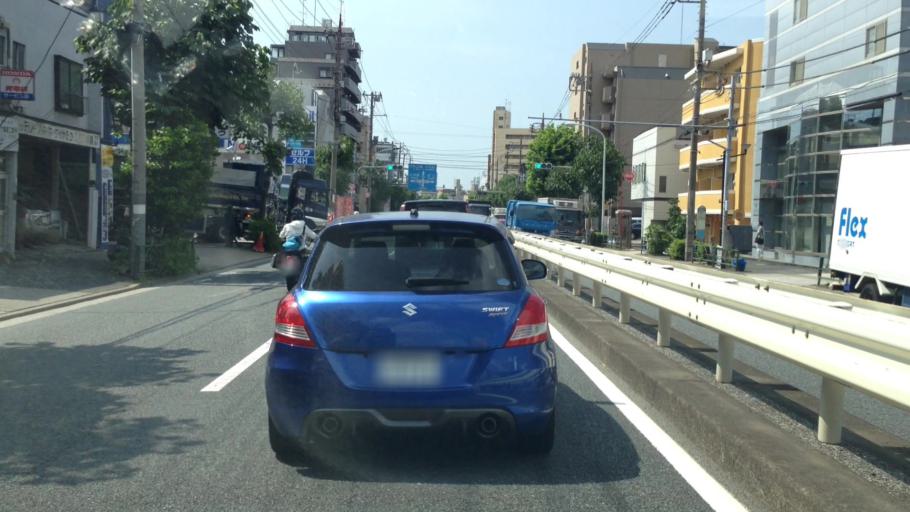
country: JP
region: Kanagawa
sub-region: Kawasaki-shi
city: Kawasaki
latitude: 35.5860
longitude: 139.7198
